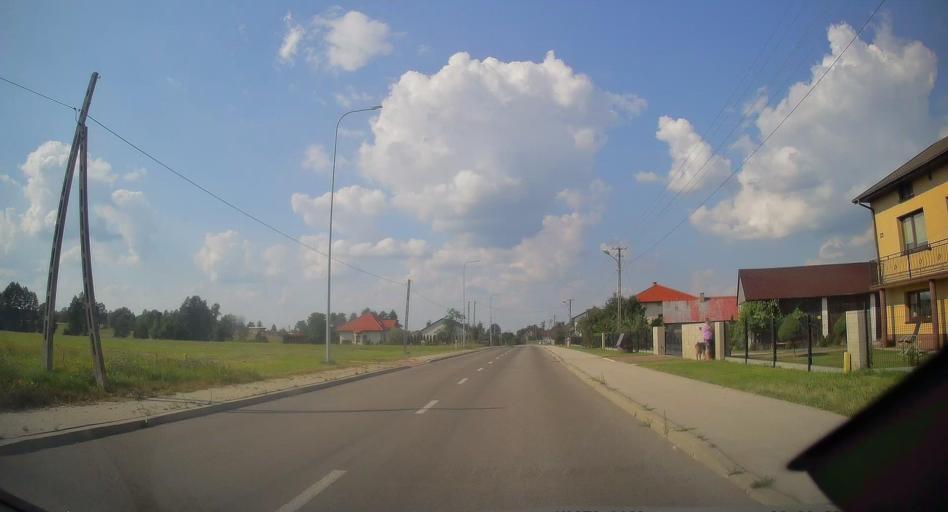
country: PL
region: Swietokrzyskie
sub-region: Powiat konecki
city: Radoszyce
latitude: 51.0284
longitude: 20.2900
